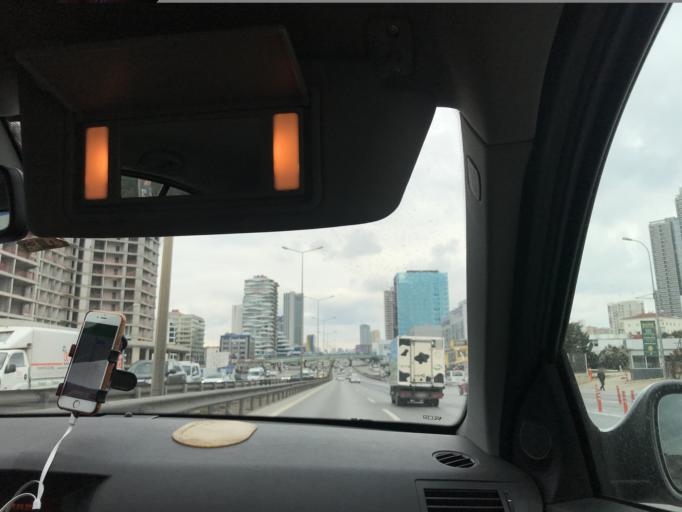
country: TR
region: Istanbul
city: Pendik
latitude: 40.8934
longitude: 29.2315
